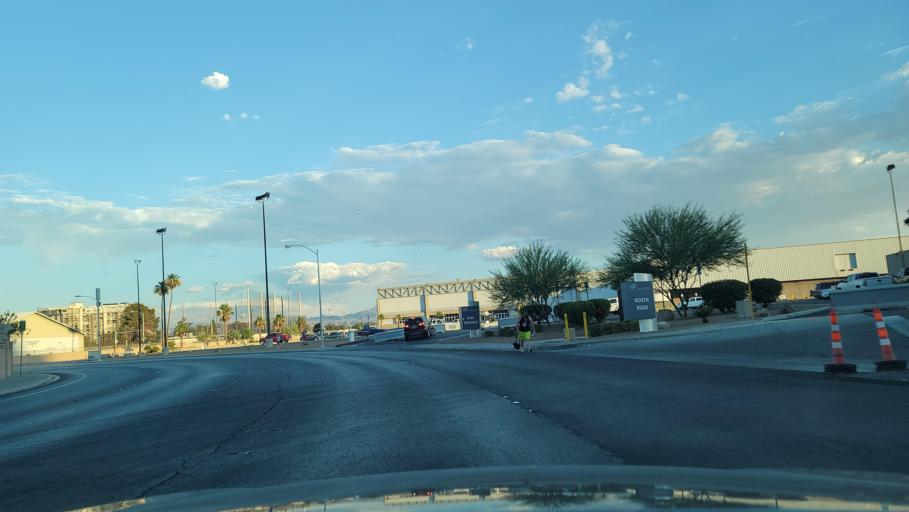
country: US
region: Nevada
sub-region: Clark County
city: Winchester
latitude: 36.1341
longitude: -115.1491
